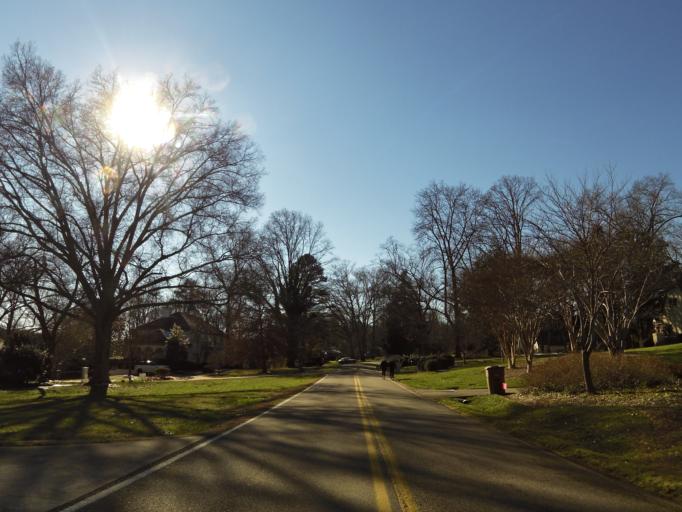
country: US
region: Tennessee
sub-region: Knox County
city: Knoxville
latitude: 35.9217
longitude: -84.0085
